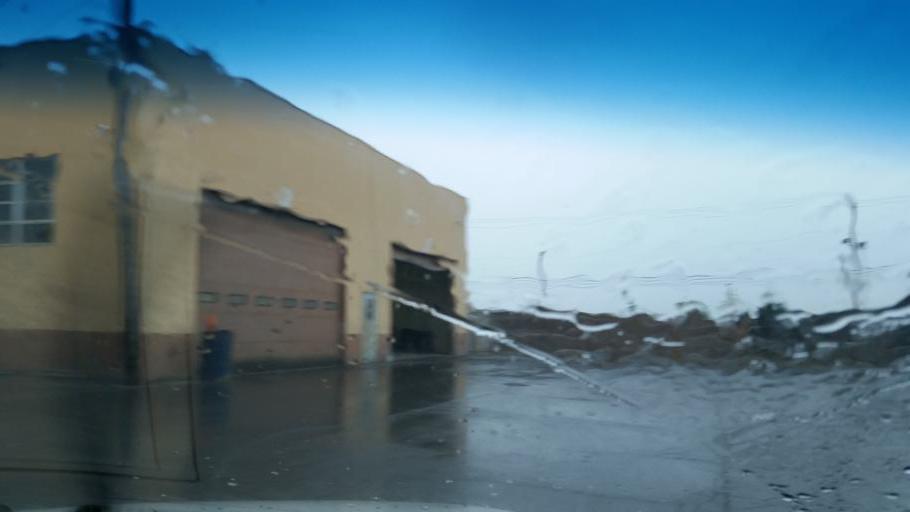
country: US
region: Indiana
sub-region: Howard County
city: Kokomo
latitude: 40.4631
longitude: -86.1228
